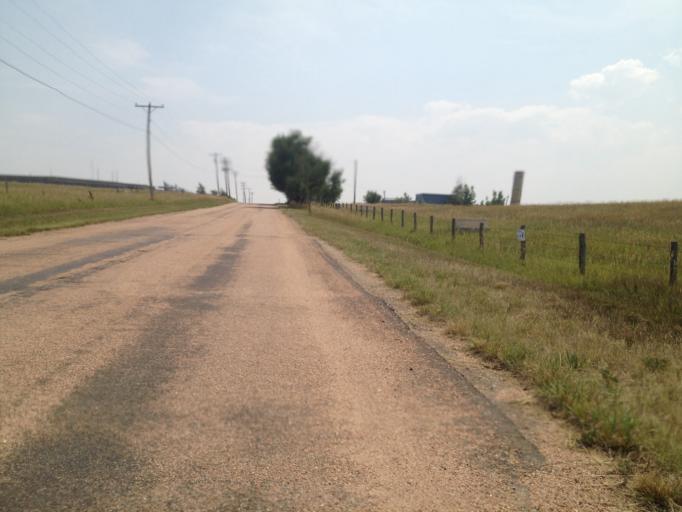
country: US
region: Colorado
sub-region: Boulder County
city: Superior
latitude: 39.9530
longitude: -105.1988
